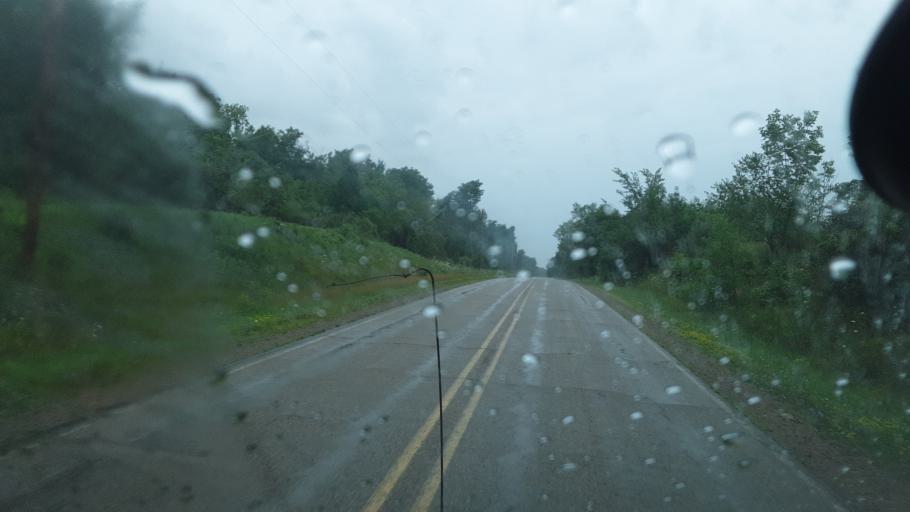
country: US
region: Ohio
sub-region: Williams County
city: Pioneer
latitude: 41.7087
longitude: -84.6736
